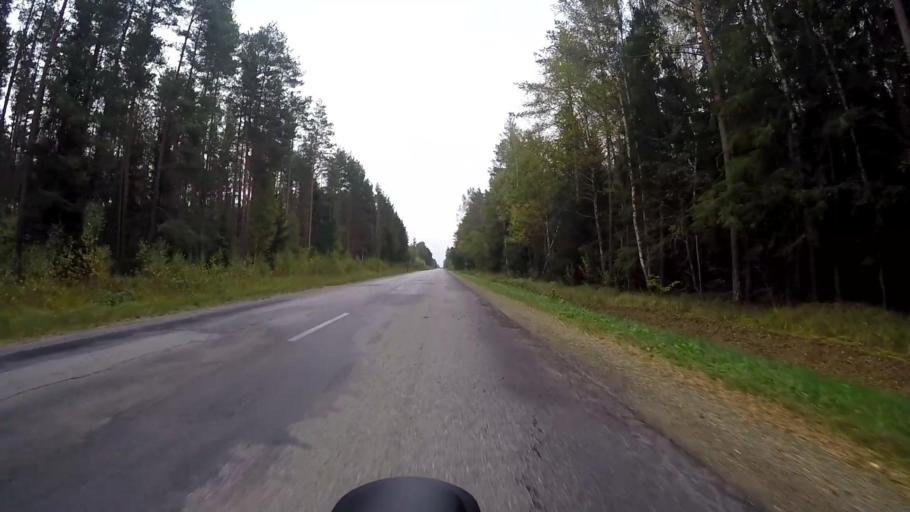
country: LV
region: Saulkrastu
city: Saulkrasti
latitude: 57.2709
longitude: 24.4755
